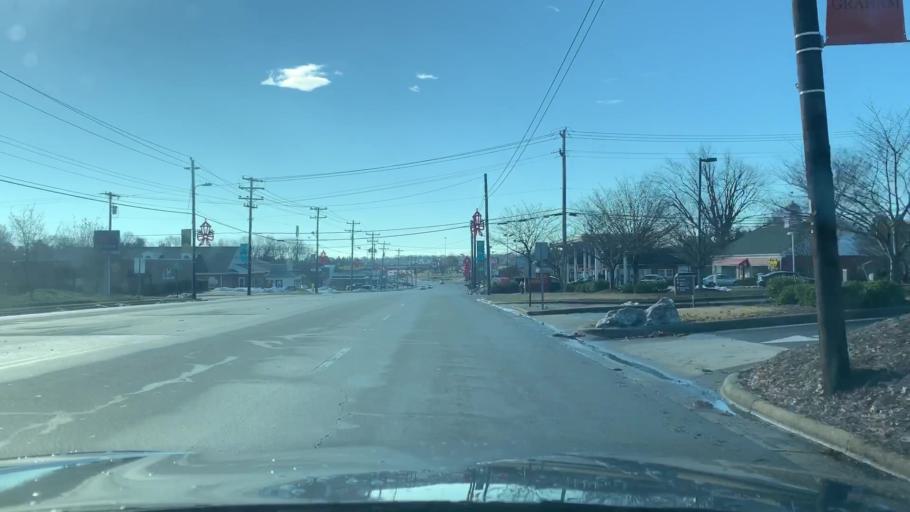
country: US
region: North Carolina
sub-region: Alamance County
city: Graham
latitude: 36.0659
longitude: -79.4005
